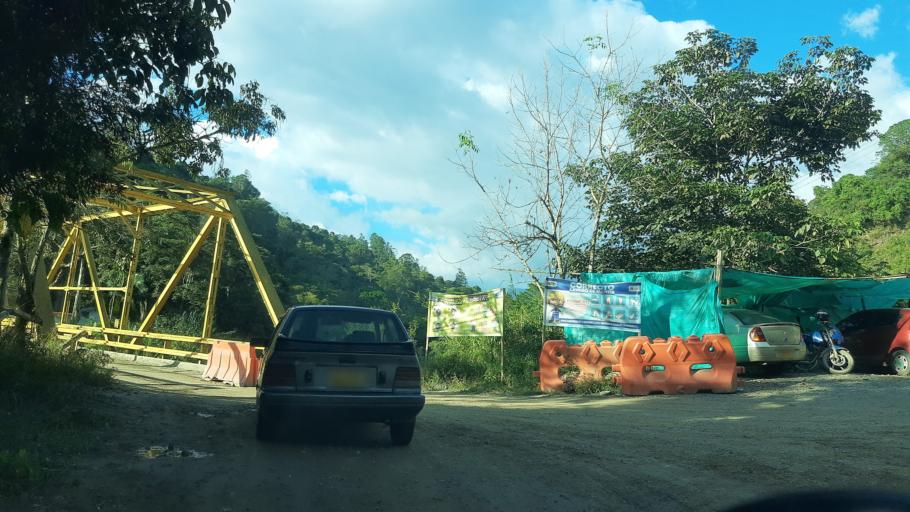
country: CO
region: Boyaca
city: Garagoa
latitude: 5.0869
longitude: -73.3808
